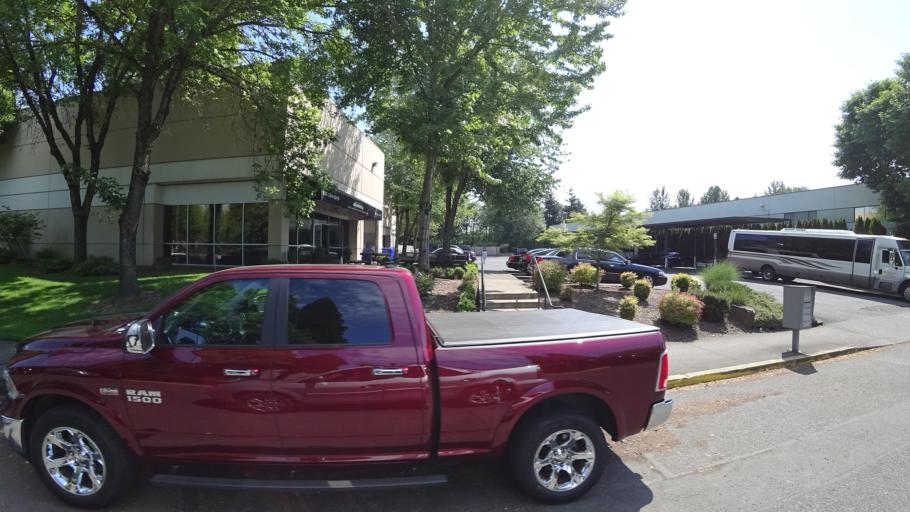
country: US
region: Oregon
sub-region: Multnomah County
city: Lents
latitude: 45.5654
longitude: -122.5411
